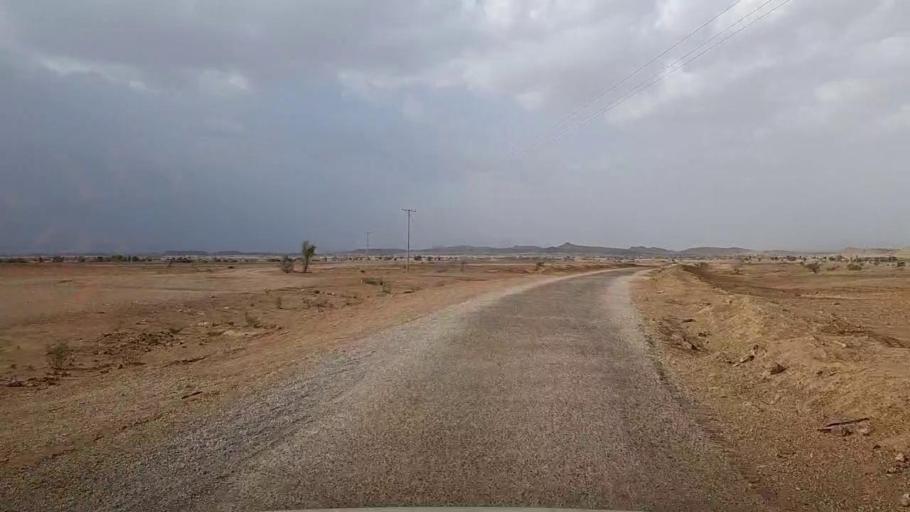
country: PK
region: Sindh
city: Jamshoro
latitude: 25.5019
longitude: 67.6340
